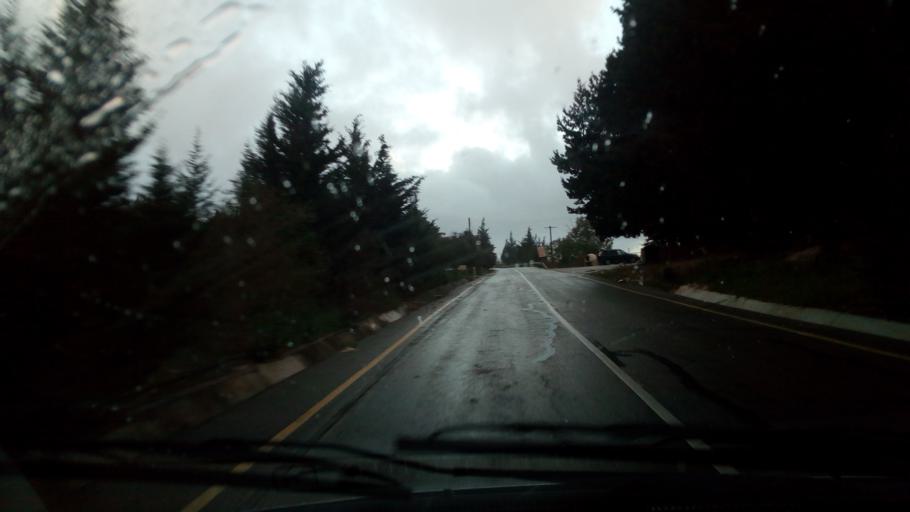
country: CY
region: Pafos
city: Polis
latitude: 34.9616
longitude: 32.4066
